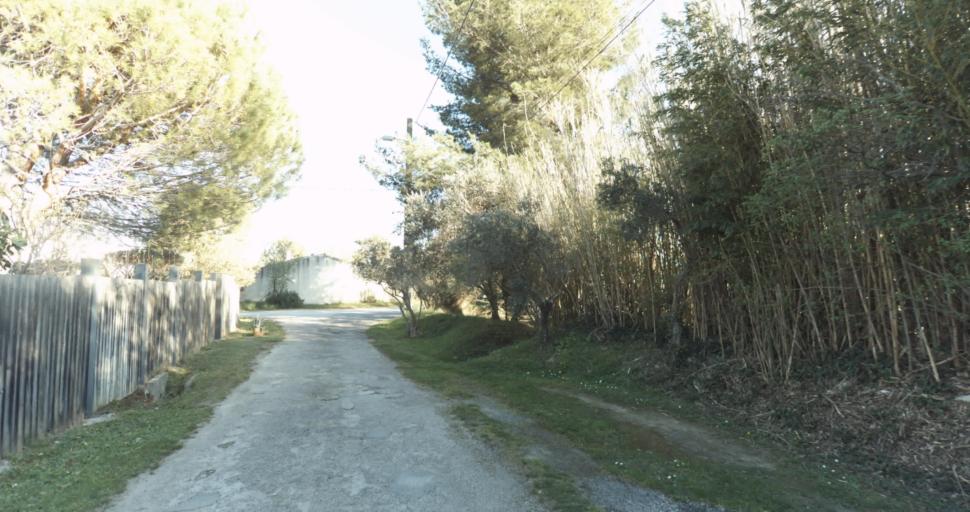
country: FR
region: Provence-Alpes-Cote d'Azur
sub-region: Departement des Bouches-du-Rhone
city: Pelissanne
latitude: 43.6382
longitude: 5.1498
